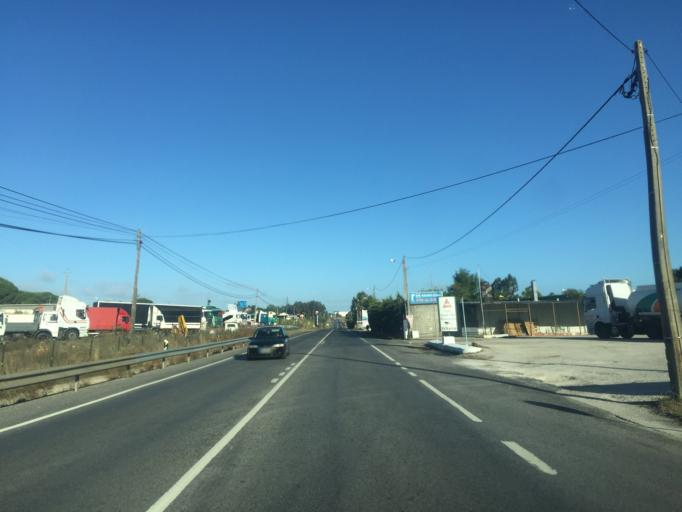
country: PT
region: Lisbon
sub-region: Azambuja
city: Aveiras de Cima
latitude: 39.1555
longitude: -8.9123
